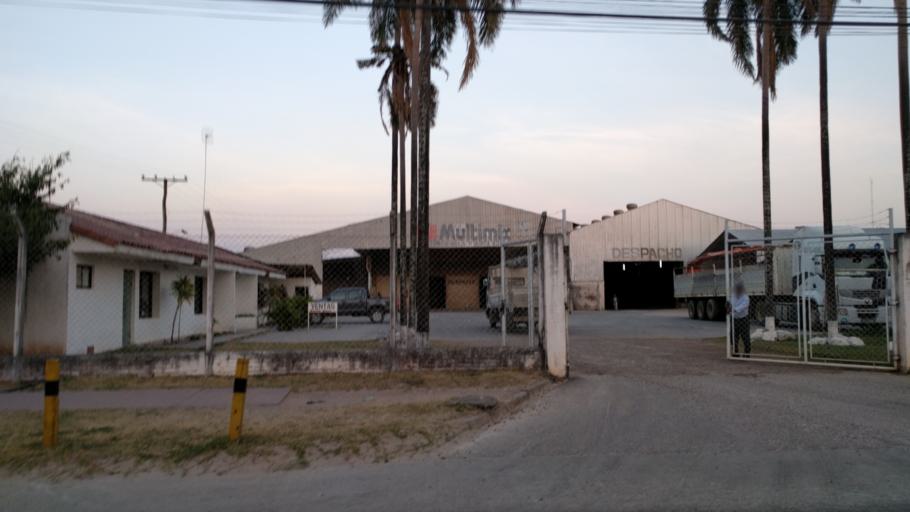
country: BO
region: Santa Cruz
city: Santa Cruz de la Sierra
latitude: -17.7623
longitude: -63.1468
